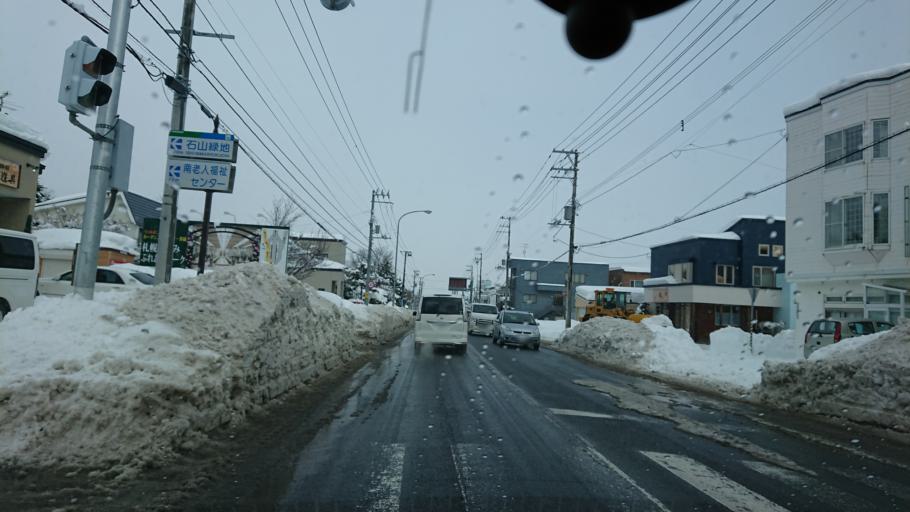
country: JP
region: Hokkaido
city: Sapporo
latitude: 42.9690
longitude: 141.3430
